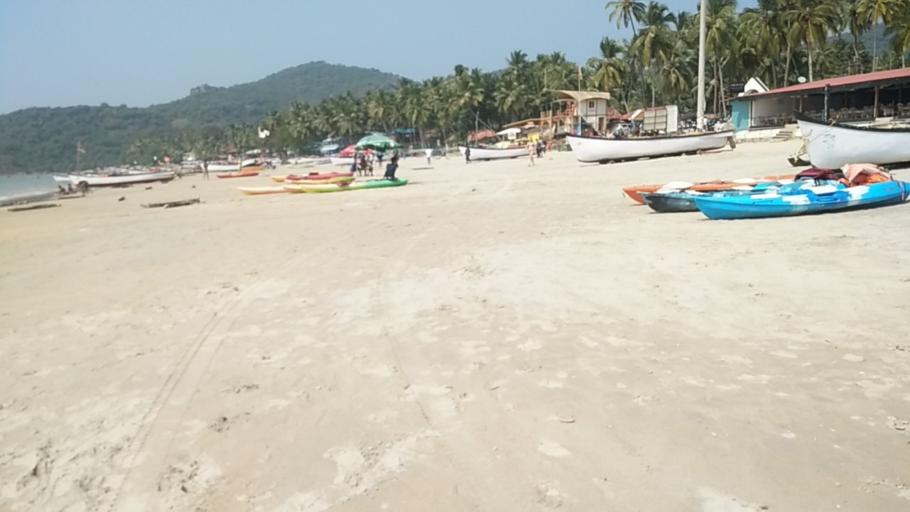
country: IN
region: Goa
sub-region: South Goa
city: Kankon
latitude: 15.0109
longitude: 74.0218
